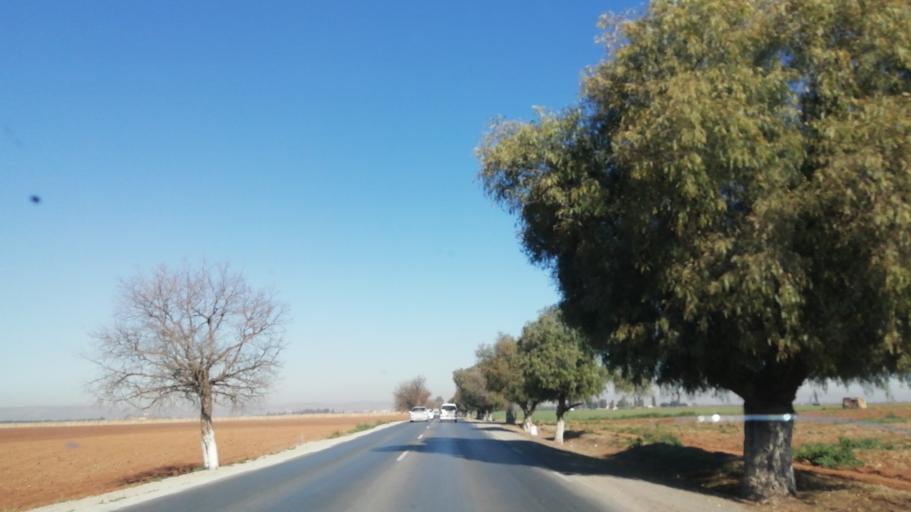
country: DZ
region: Mascara
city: Mascara
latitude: 35.2777
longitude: 0.1283
